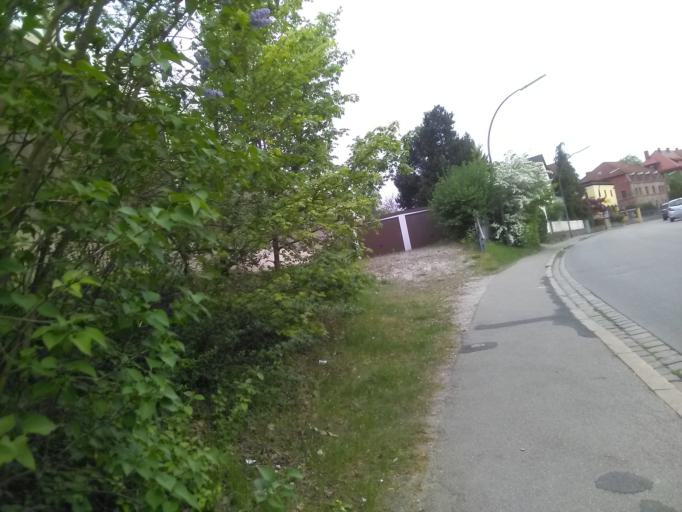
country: DE
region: Bavaria
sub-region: Regierungsbezirk Mittelfranken
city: Roth
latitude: 49.2439
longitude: 11.0834
